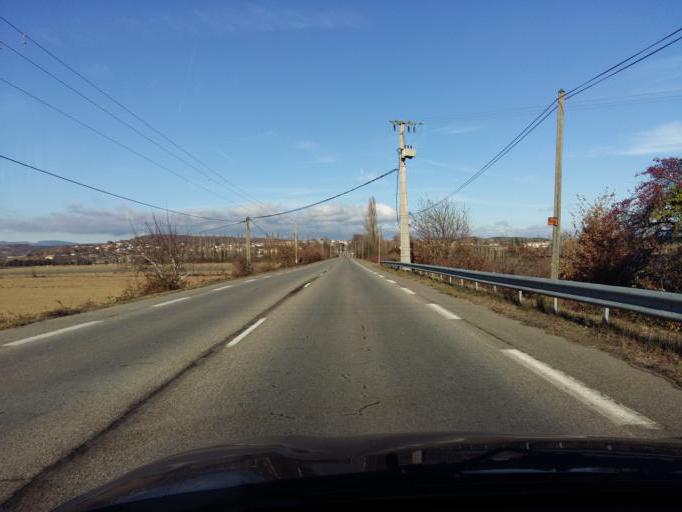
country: FR
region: Rhone-Alpes
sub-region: Departement de l'Ardeche
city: Saint-Just-d'Ardeche
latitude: 44.2895
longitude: 4.6140
